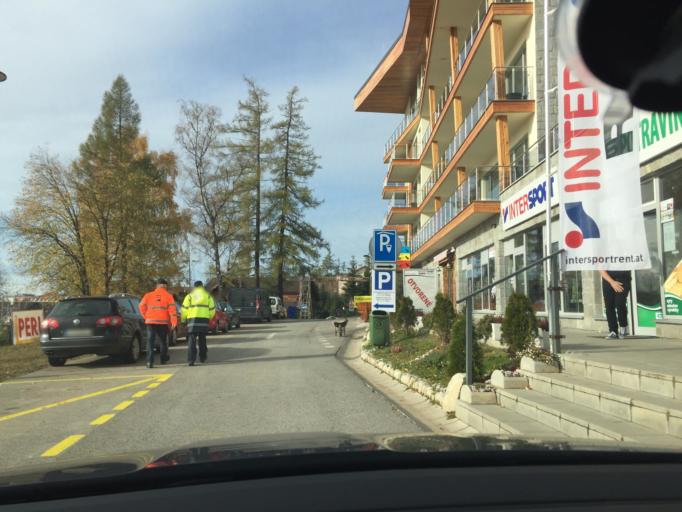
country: SK
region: Presovsky
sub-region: Okres Poprad
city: Vysoke Tatry
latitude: 49.1408
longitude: 20.2197
